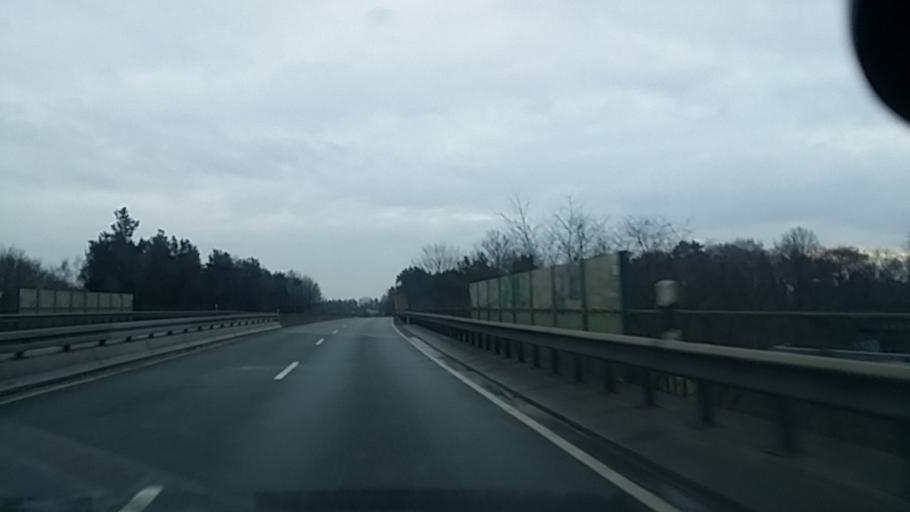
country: DE
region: Lower Saxony
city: Meppen
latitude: 52.7091
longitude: 7.2916
